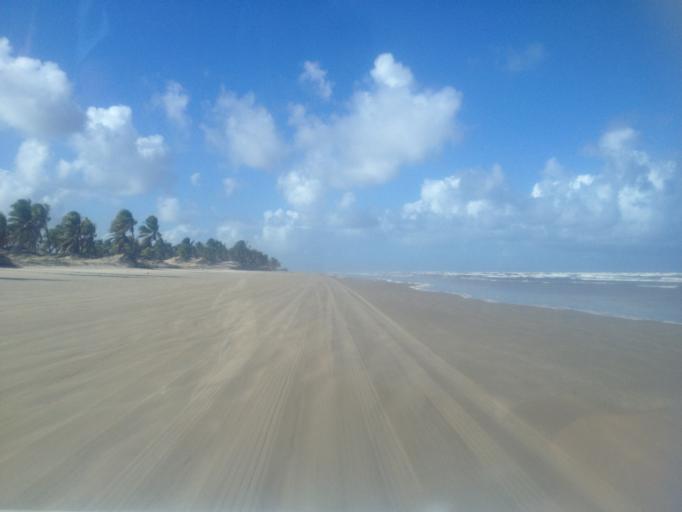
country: BR
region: Sergipe
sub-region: Indiaroba
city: Indiaroba
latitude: -11.4736
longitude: -37.3601
